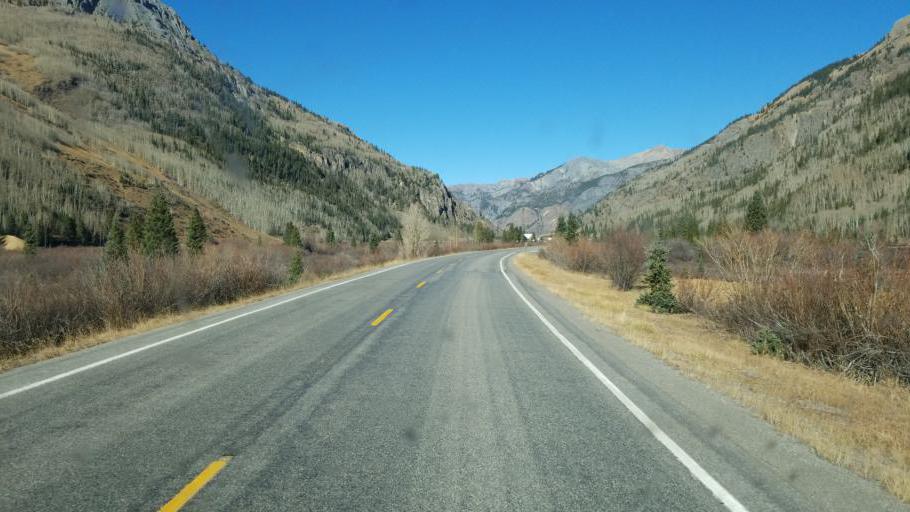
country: US
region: Colorado
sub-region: Ouray County
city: Ouray
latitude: 37.9477
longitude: -107.6675
